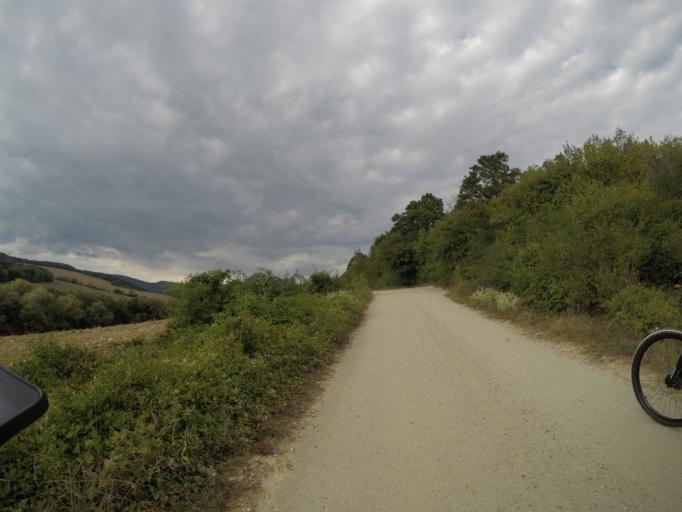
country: SK
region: Trenciansky
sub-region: Okres Trencin
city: Trencin
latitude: 48.9108
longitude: 17.9997
